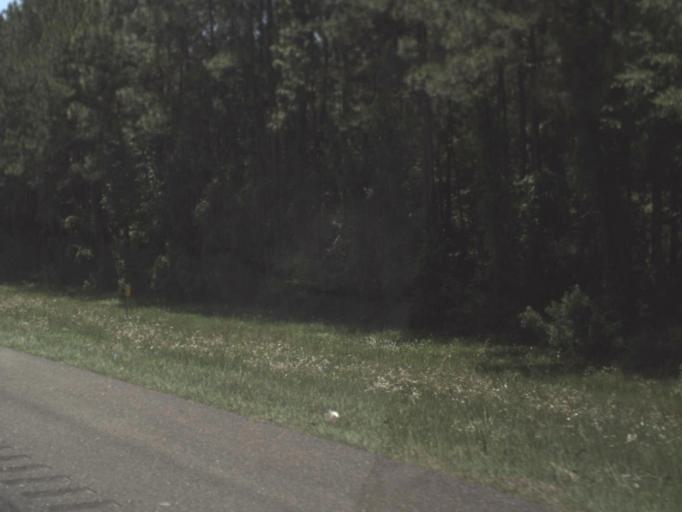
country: US
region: Florida
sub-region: Nassau County
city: Nassau Village-Ratliff
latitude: 30.4253
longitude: -81.7329
